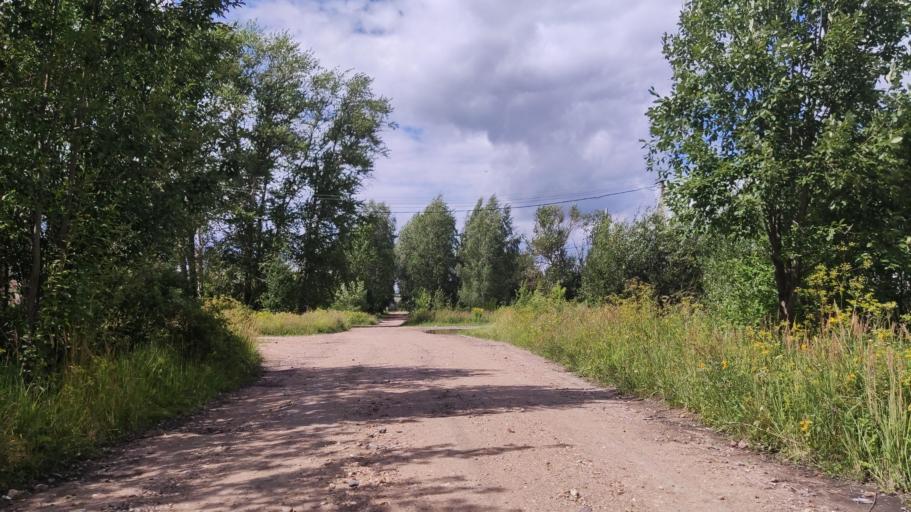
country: RU
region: Tverskaya
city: Rzhev
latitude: 56.2401
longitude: 34.3051
